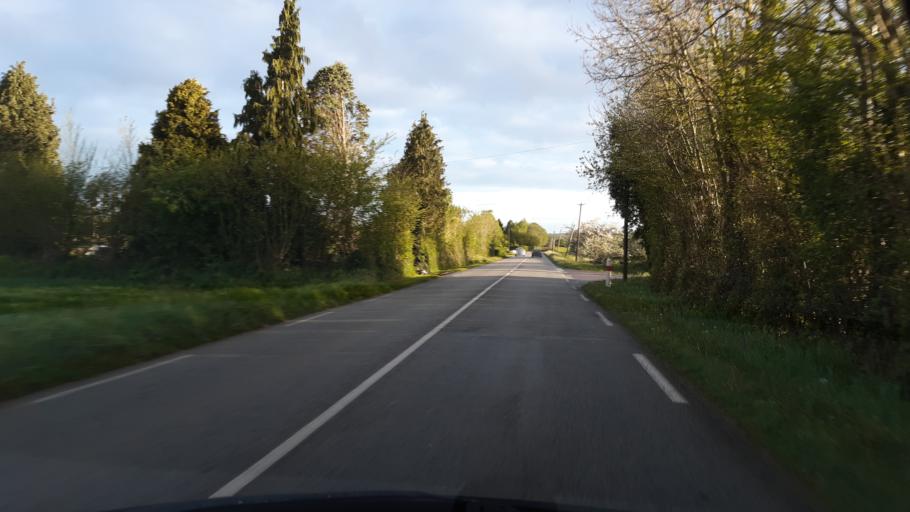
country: FR
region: Lower Normandy
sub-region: Departement de la Manche
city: Agneaux
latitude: 49.0559
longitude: -1.1325
